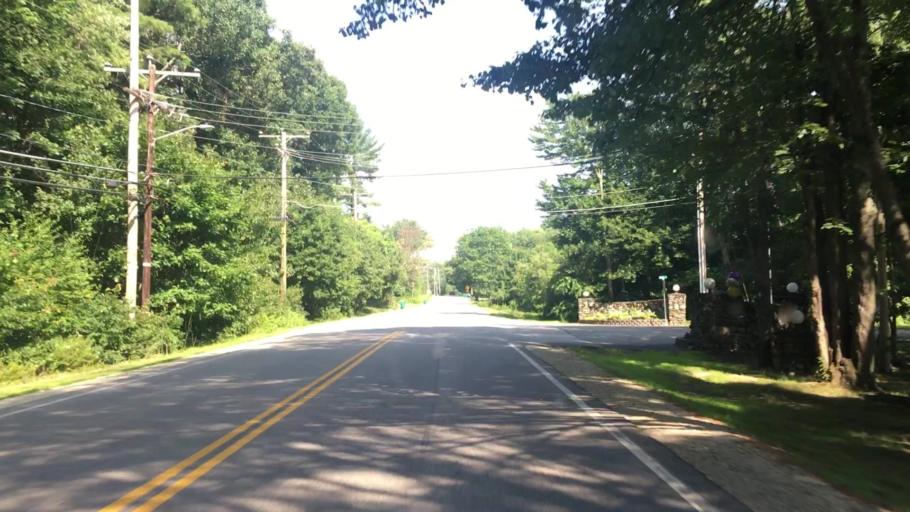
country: US
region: New Hampshire
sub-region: Strafford County
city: Rochester
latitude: 43.2694
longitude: -70.9459
